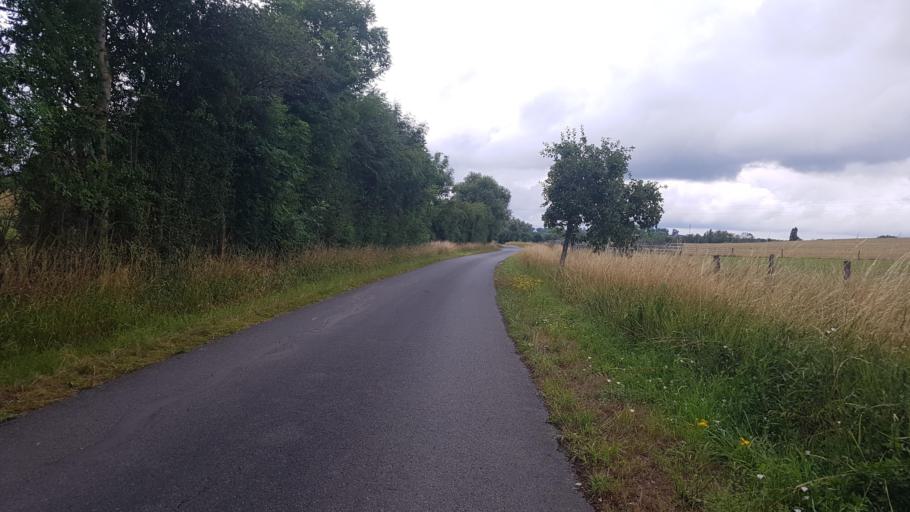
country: FR
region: Lorraine
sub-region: Departement de la Moselle
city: Lorquin
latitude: 48.7080
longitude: 7.0062
